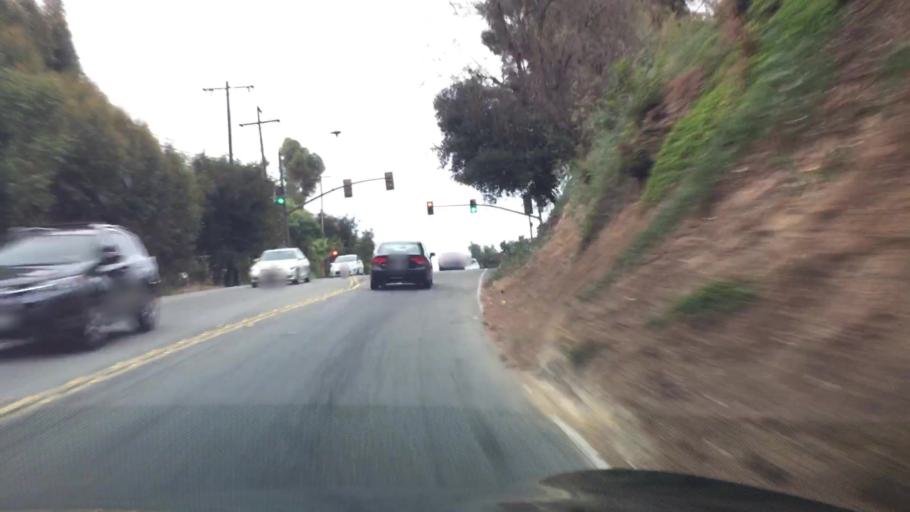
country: US
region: California
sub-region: Los Angeles County
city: La Habra Heights
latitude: 33.9693
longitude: -117.9626
